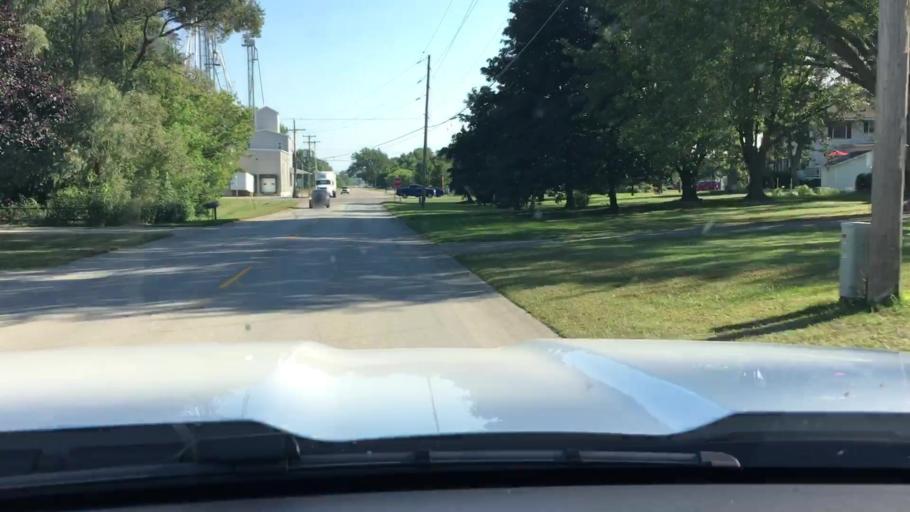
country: US
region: Michigan
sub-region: Ottawa County
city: Zeeland
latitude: 42.8129
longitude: -85.9401
